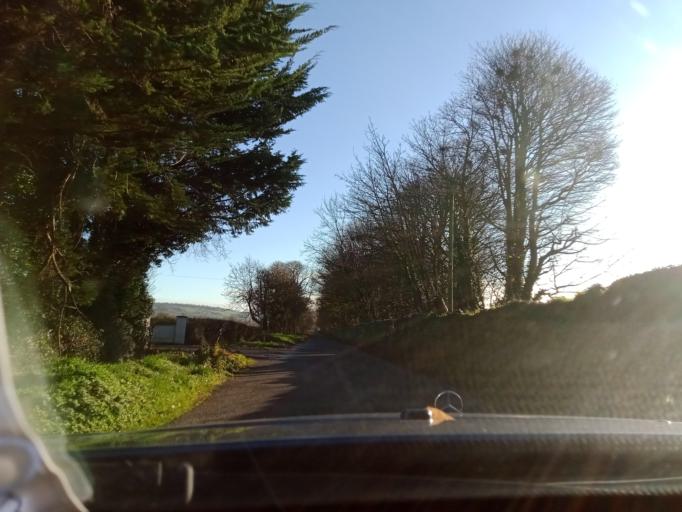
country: IE
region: Leinster
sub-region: Kilkenny
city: Piltown
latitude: 52.3631
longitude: -7.3167
